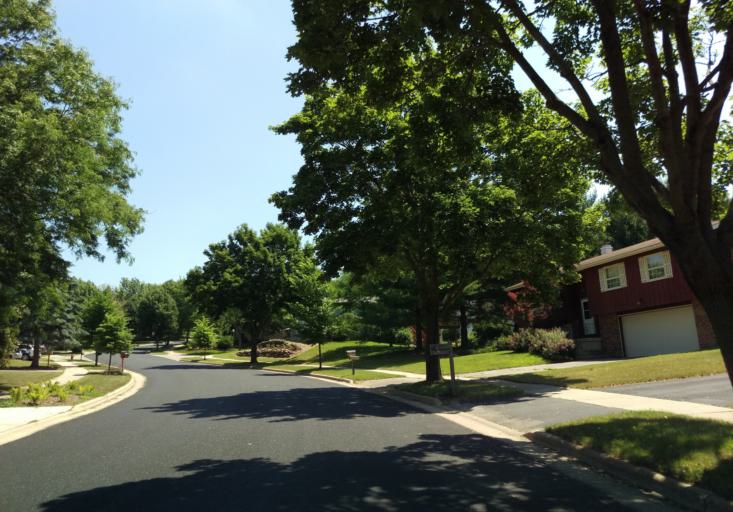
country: US
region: Wisconsin
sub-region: Dane County
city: Verona
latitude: 43.0197
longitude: -89.5014
